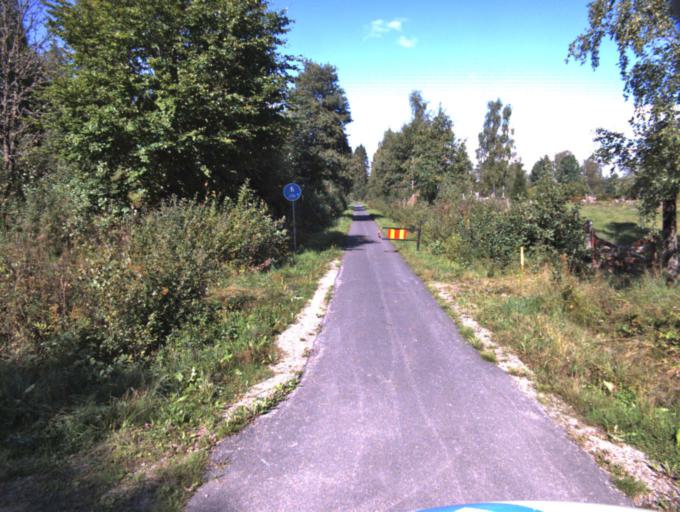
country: SE
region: Vaestra Goetaland
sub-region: Ulricehamns Kommun
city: Ulricehamn
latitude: 57.8121
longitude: 13.3547
